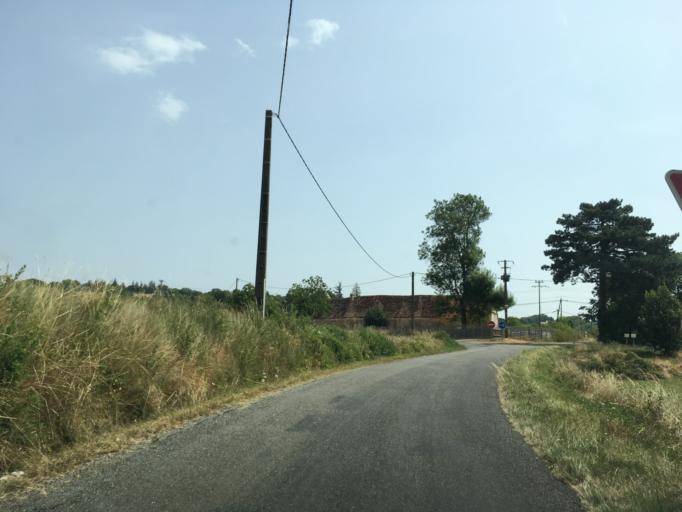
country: FR
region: Midi-Pyrenees
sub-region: Departement du Lot
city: Le Vigan
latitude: 44.7478
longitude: 1.4981
